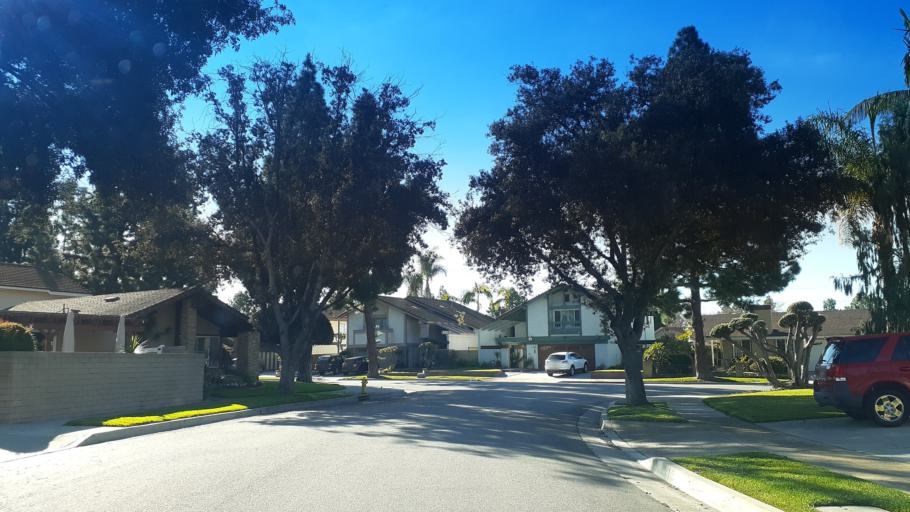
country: US
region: California
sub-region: Los Angeles County
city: Cerritos
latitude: 33.8526
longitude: -118.0673
